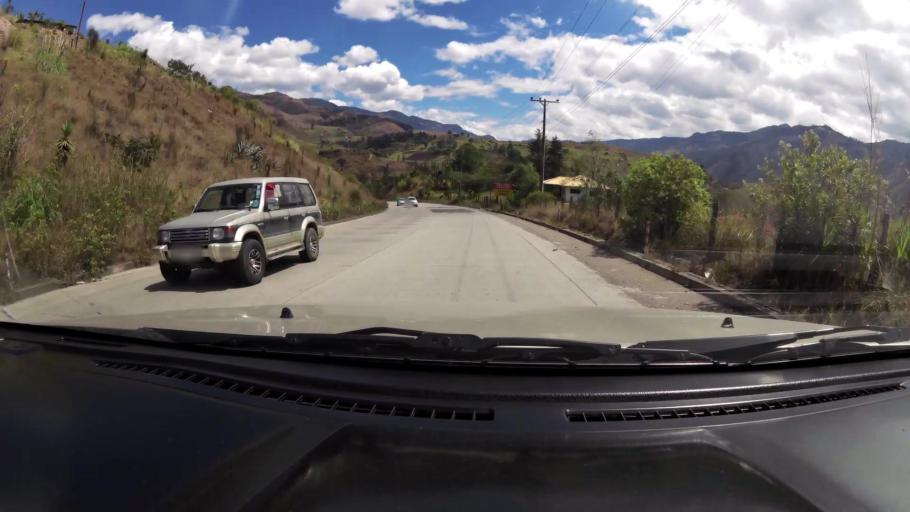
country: EC
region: Azuay
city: Cuenca
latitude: -3.1979
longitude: -79.1808
